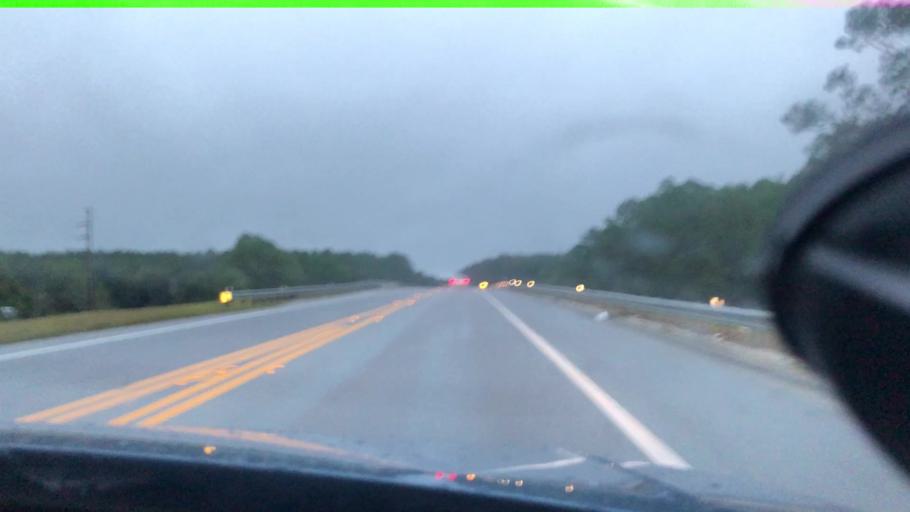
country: US
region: Florida
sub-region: Volusia County
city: West DeLand
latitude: 29.0241
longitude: -81.3558
